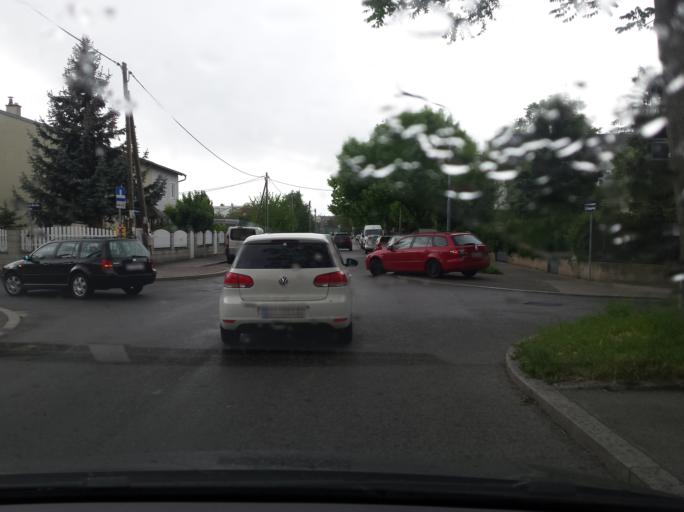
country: AT
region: Lower Austria
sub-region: Politischer Bezirk Wien-Umgebung
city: Gerasdorf bei Wien
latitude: 48.2574
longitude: 16.4237
